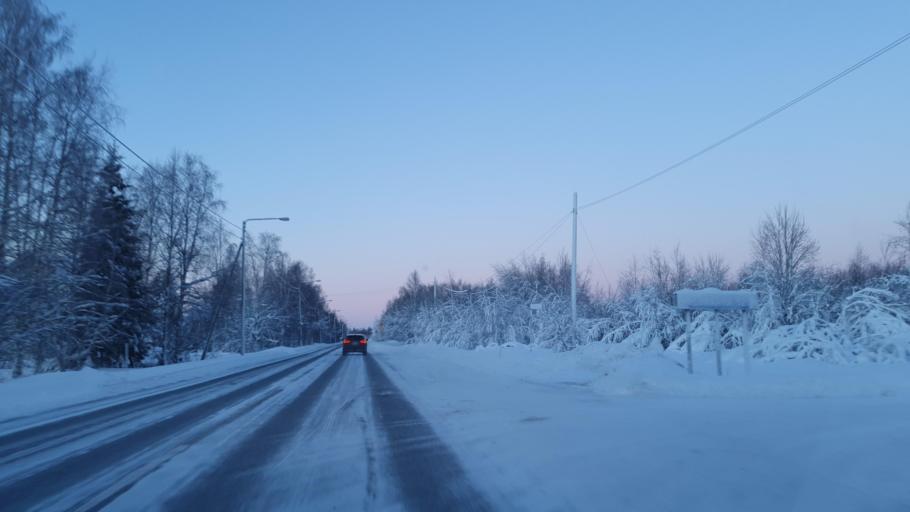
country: FI
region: Lapland
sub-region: Kemi-Tornio
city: Tornio
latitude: 66.0595
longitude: 23.9980
